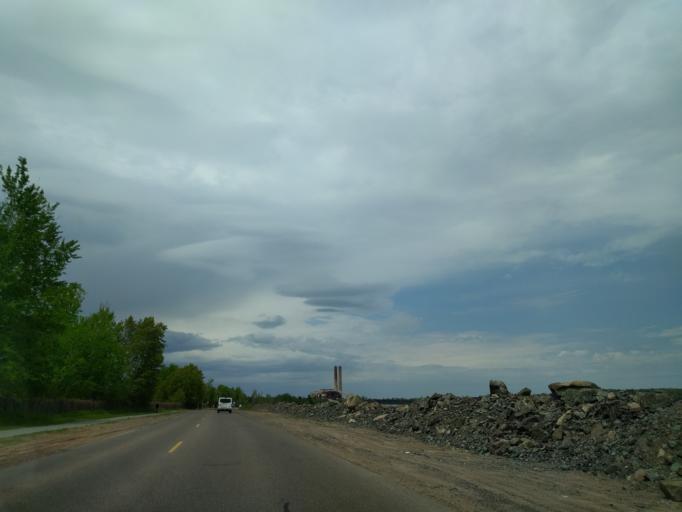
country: US
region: Michigan
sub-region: Marquette County
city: Marquette
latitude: 46.5640
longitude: -87.3896
